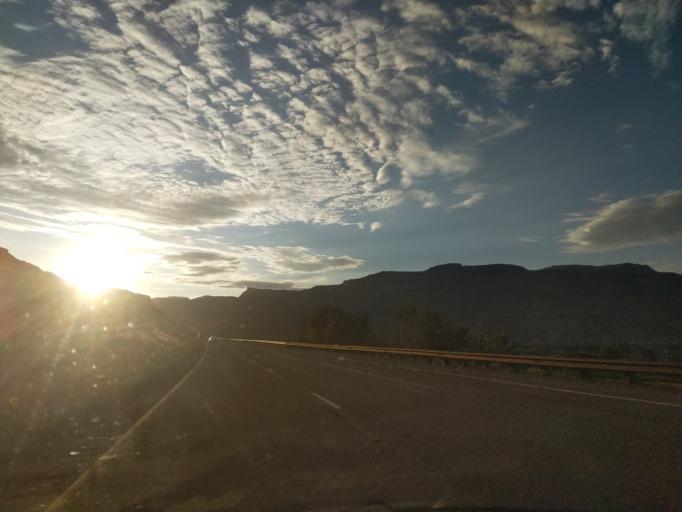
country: US
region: Colorado
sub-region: Mesa County
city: Palisade
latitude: 39.1166
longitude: -108.3513
